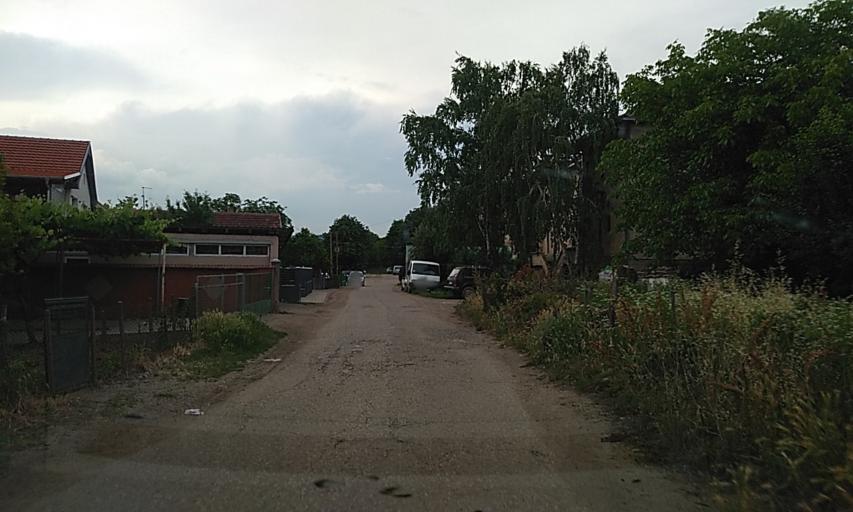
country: RS
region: Central Serbia
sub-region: Nisavski Okrug
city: Nis
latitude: 43.3329
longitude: 21.8350
